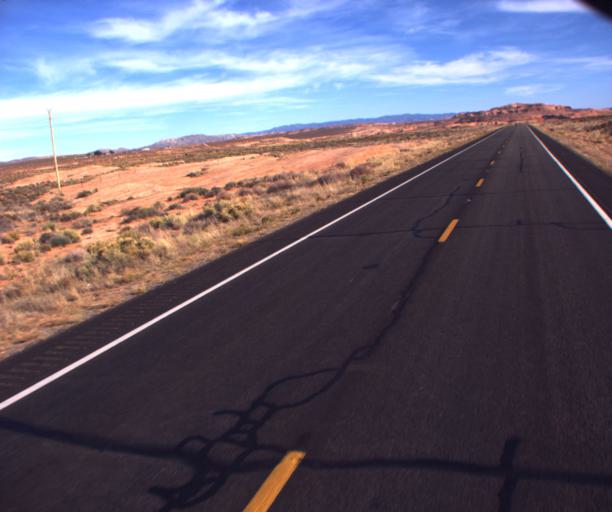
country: US
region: Arizona
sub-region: Apache County
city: Many Farms
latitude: 36.9307
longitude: -109.6247
